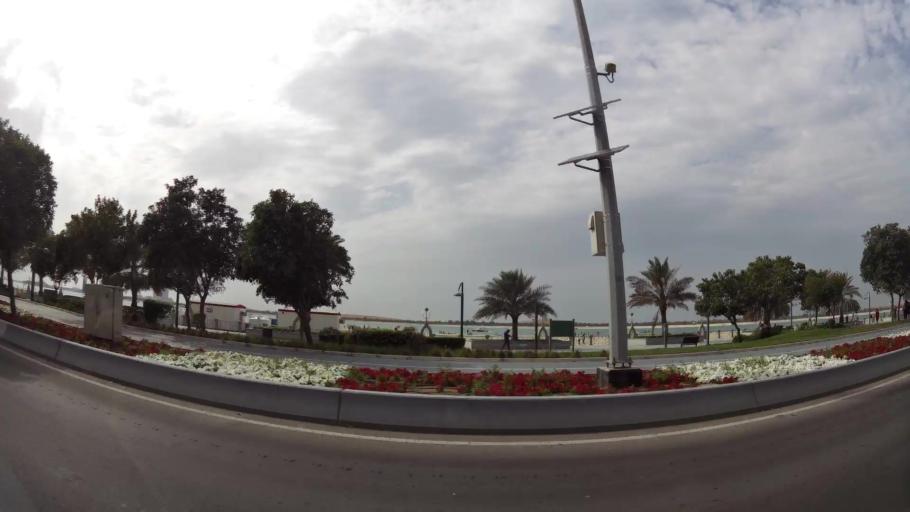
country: AE
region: Abu Dhabi
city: Abu Dhabi
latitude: 24.4880
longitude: 54.3502
